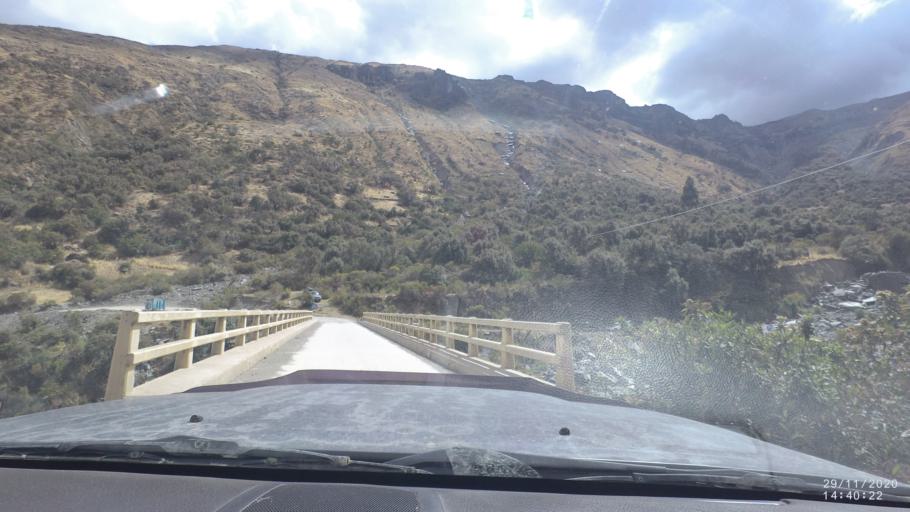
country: BO
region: Cochabamba
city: Sipe Sipe
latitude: -17.2751
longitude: -66.3303
